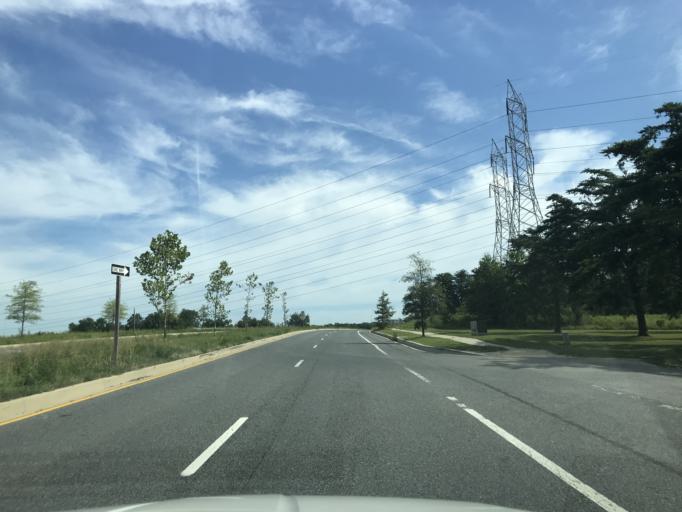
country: US
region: Maryland
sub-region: Prince George's County
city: West Laurel
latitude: 39.0717
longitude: -76.8872
